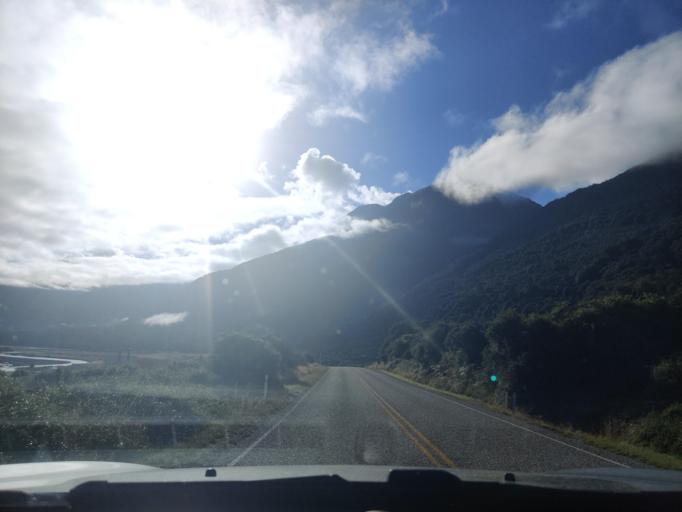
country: NZ
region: Otago
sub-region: Queenstown-Lakes District
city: Wanaka
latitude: -44.1610
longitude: 169.2852
